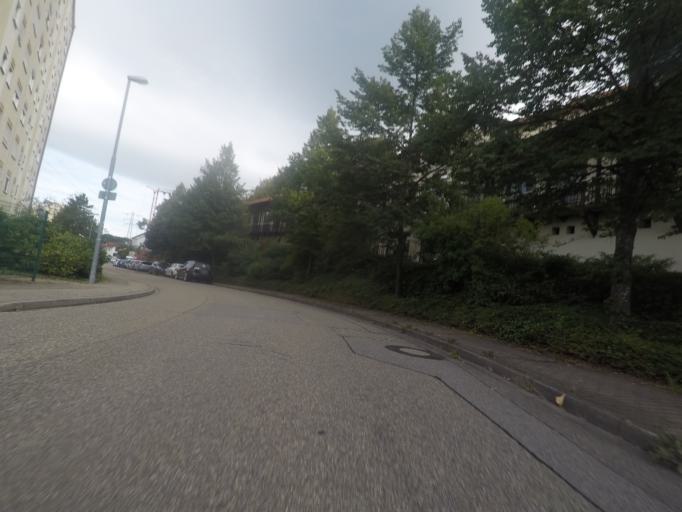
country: DE
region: Baden-Wuerttemberg
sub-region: Karlsruhe Region
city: Gernsbach
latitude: 48.7684
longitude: 8.3473
